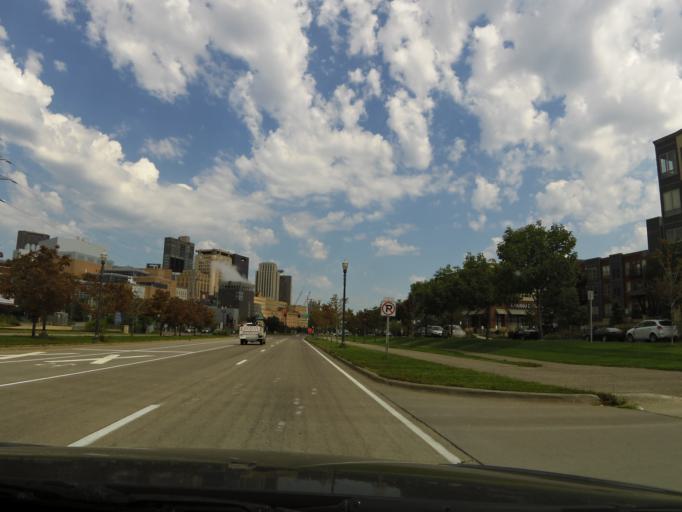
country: US
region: Minnesota
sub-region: Ramsey County
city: Saint Paul
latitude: 44.9399
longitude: -93.1011
